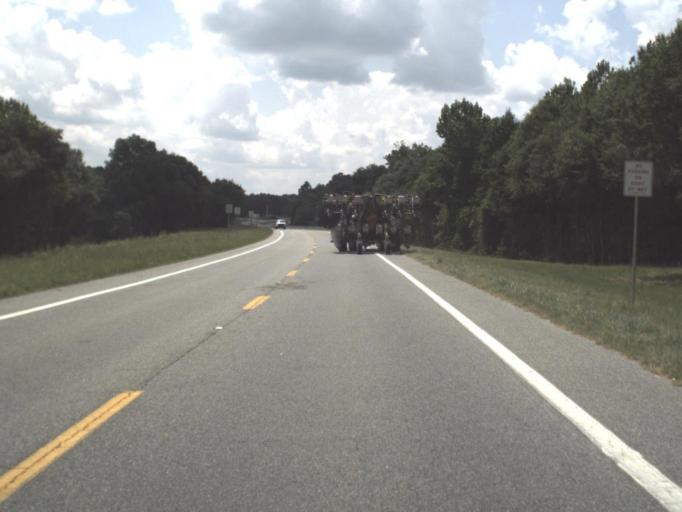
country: US
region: Florida
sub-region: Hamilton County
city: Jasper
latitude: 30.5280
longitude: -83.0352
